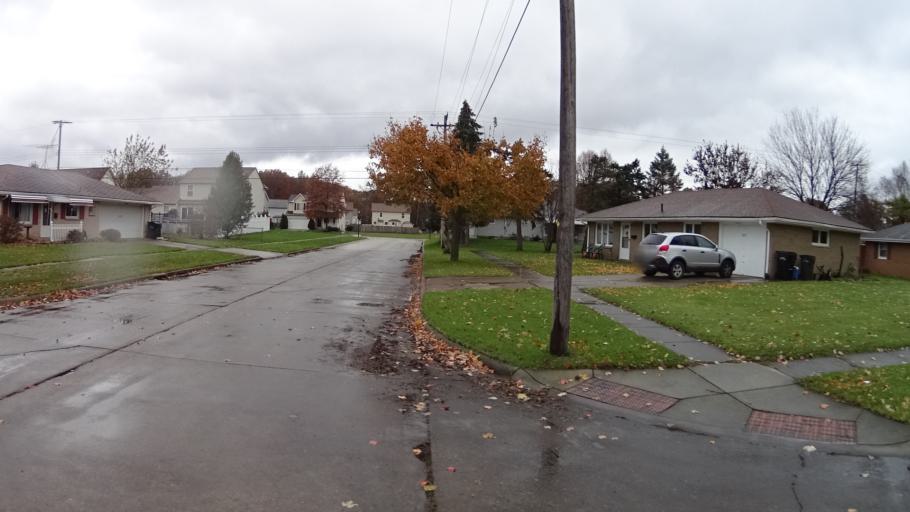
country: US
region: Ohio
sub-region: Lorain County
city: Elyria
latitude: 41.3829
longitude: -82.1392
